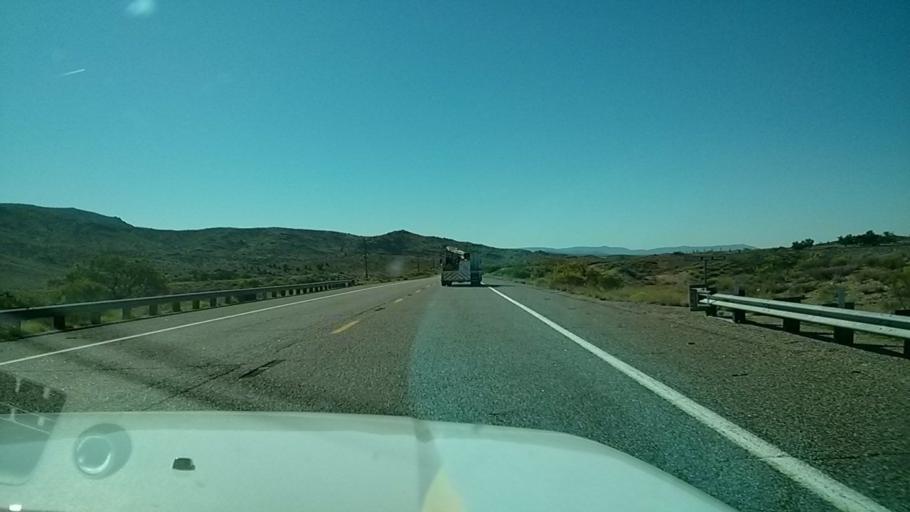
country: US
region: Arizona
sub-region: Mohave County
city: New Kingman-Butler
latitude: 35.3907
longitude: -113.7425
